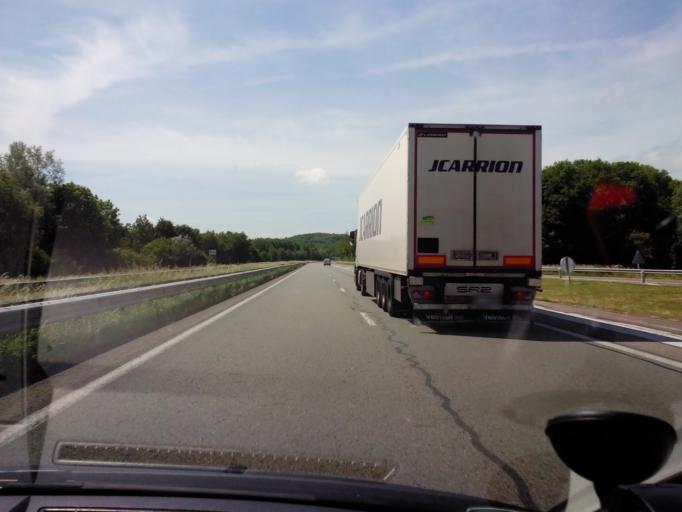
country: FR
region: Champagne-Ardenne
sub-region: Departement de la Haute-Marne
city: Avrecourt
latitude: 47.9758
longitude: 5.4979
